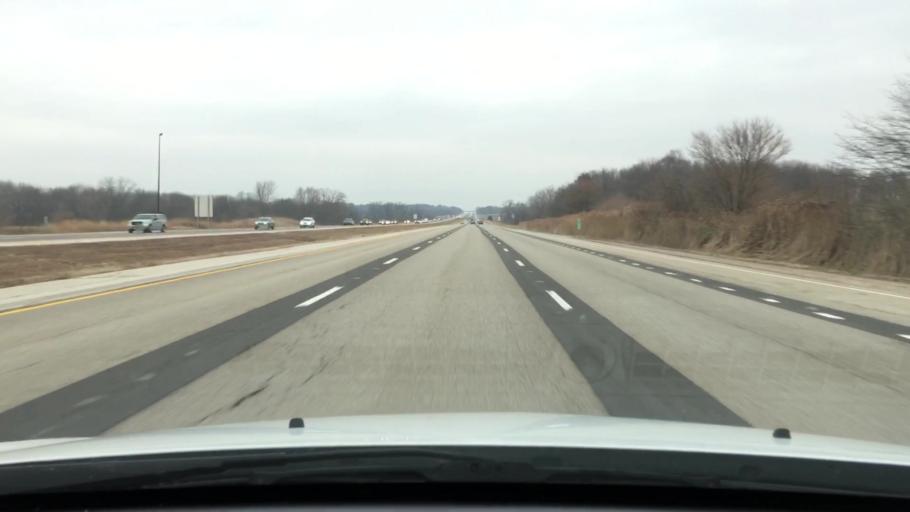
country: US
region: Illinois
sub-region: Logan County
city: Lincoln
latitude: 40.1176
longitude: -89.4164
